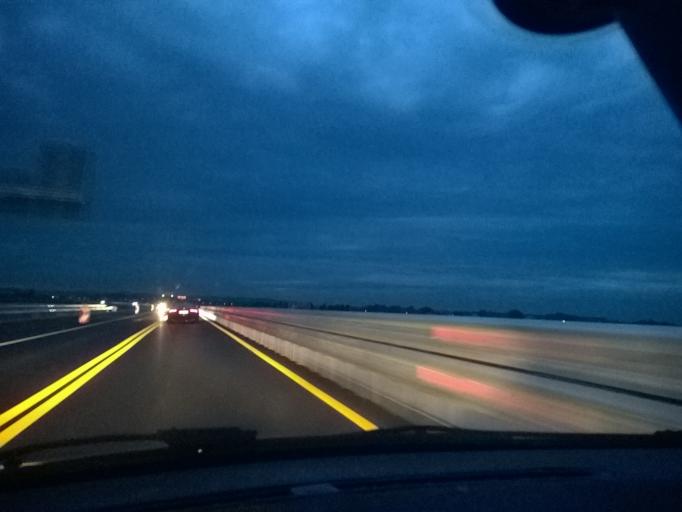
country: SI
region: Hajdina
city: Spodnja Hajdina
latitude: 46.3791
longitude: 15.8660
